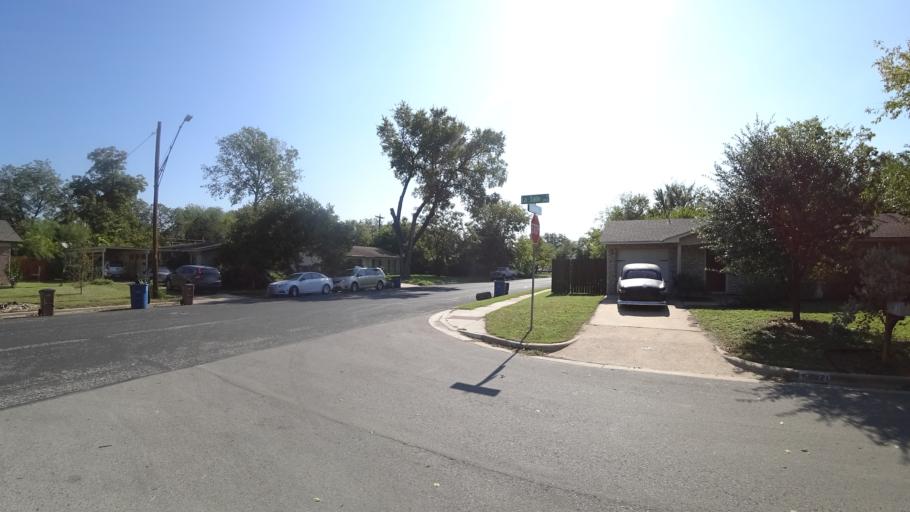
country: US
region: Texas
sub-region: Travis County
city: Austin
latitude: 30.3165
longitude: -97.6677
